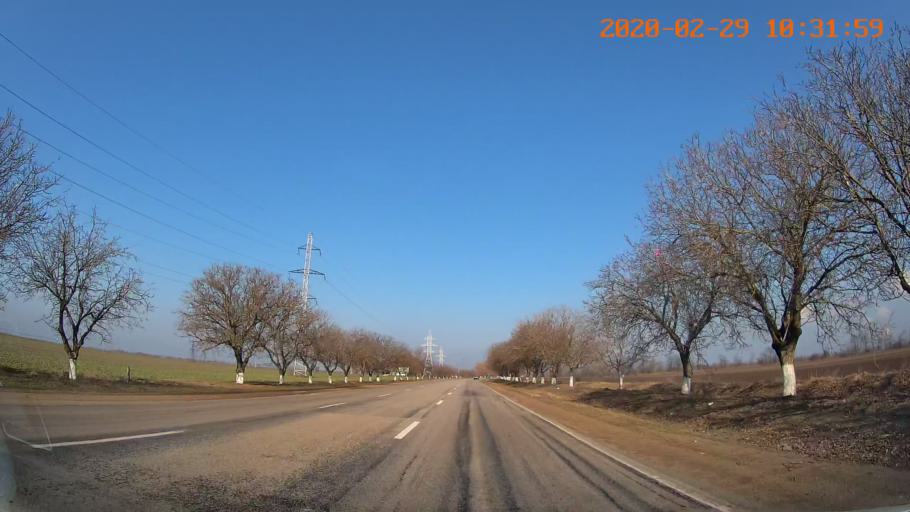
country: UA
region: Odessa
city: Velykoploske
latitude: 46.9554
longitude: 29.5579
